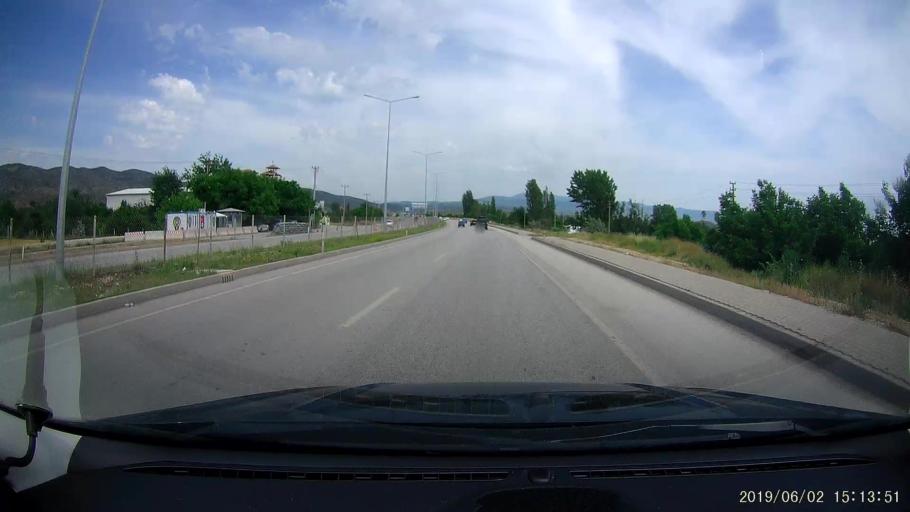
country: TR
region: Corum
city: Osmancik
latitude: 40.9706
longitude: 34.8269
